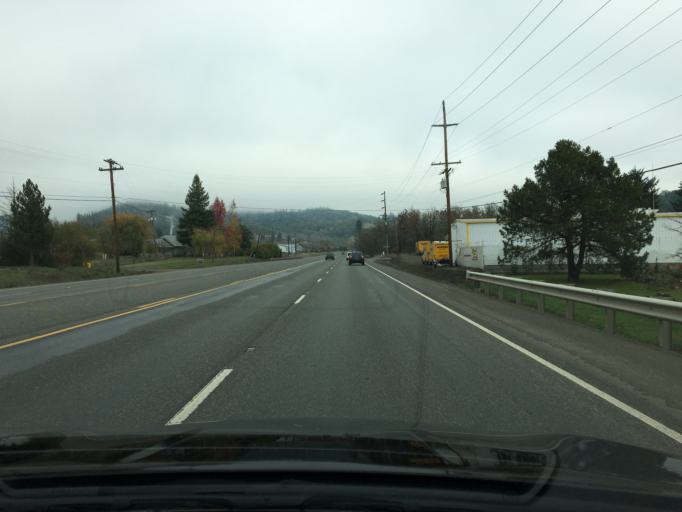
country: US
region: Oregon
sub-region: Douglas County
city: Roseburg North
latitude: 43.2166
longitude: -123.2920
